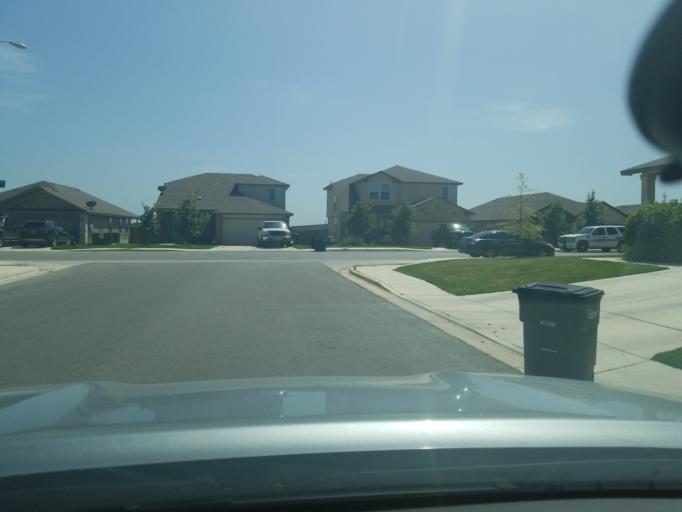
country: US
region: Texas
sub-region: Guadalupe County
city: Lake Dunlap
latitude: 29.6686
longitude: -98.0393
